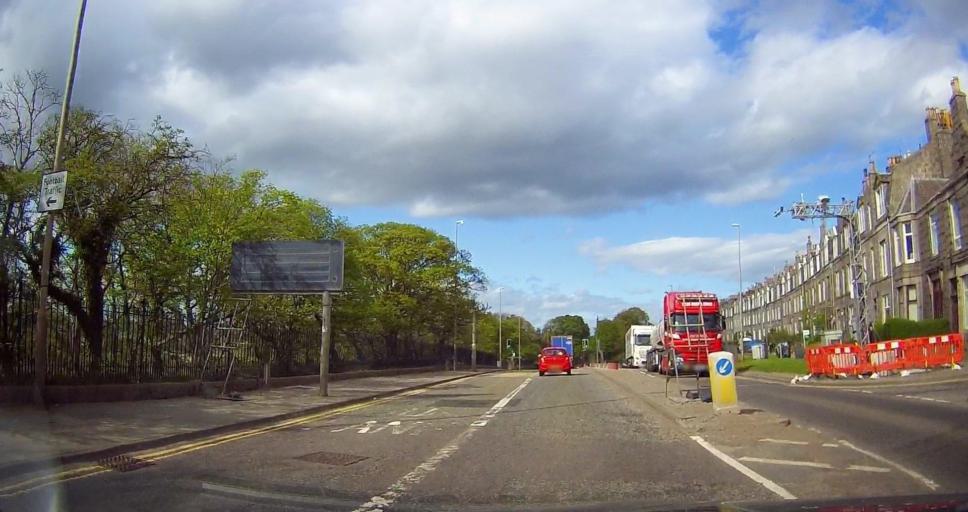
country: GB
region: Scotland
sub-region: Aberdeen City
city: Aberdeen
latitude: 57.1334
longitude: -2.0946
